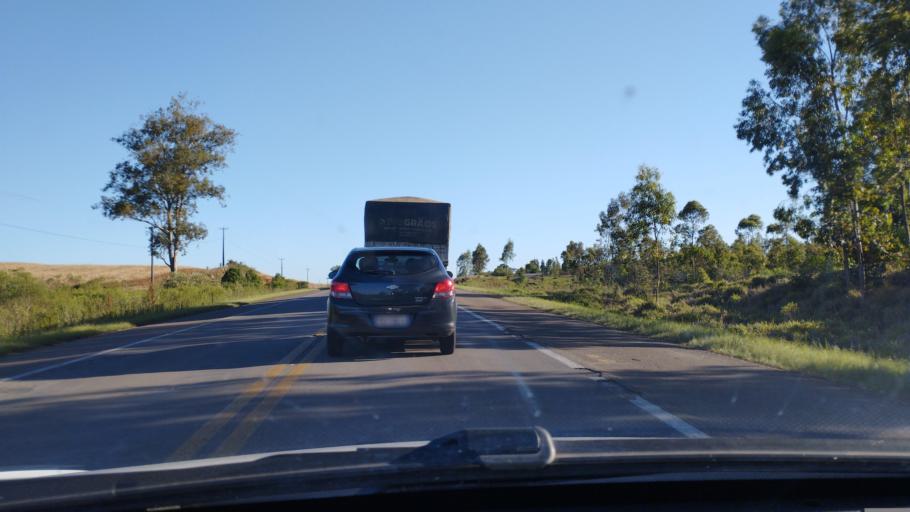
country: BR
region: Rio Grande do Sul
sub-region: Julio De Castilhos
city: Julio de Castilhos
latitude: -29.3772
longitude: -53.6706
